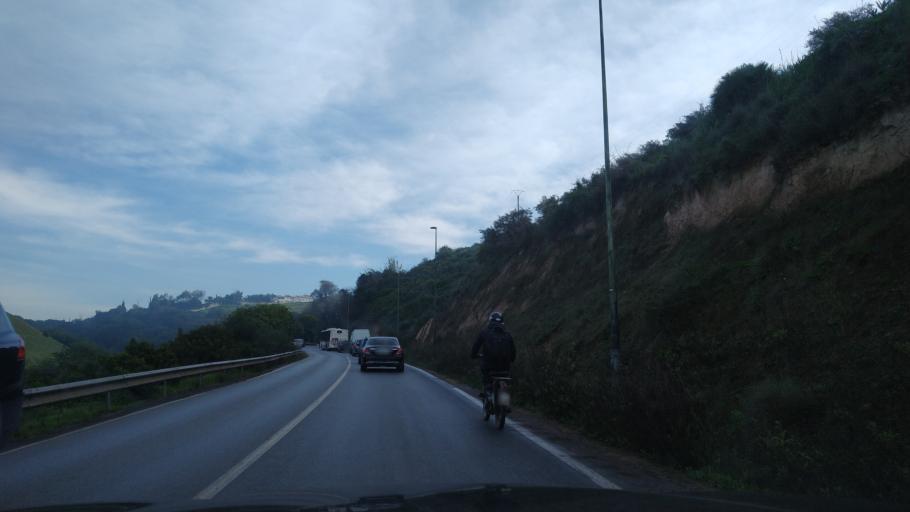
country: MA
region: Rabat-Sale-Zemmour-Zaer
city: Sale
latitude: 33.9931
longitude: -6.7595
